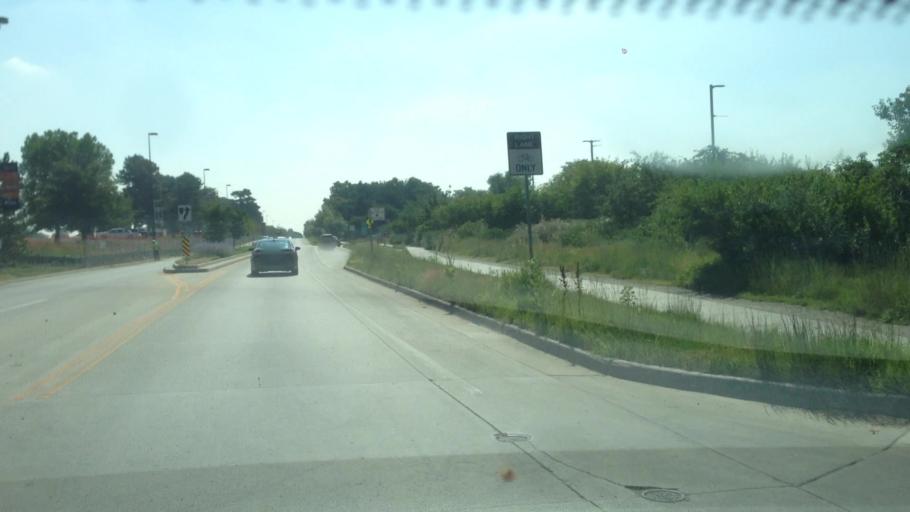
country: US
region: Colorado
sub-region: Denver County
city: Denver
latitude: 39.7512
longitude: -104.9508
